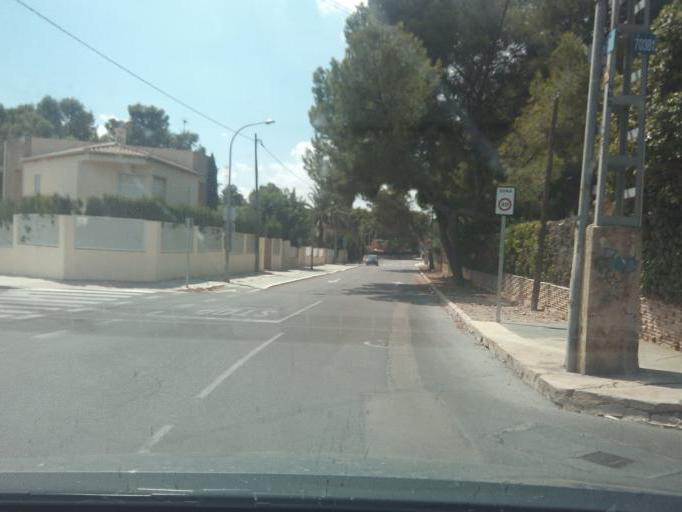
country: ES
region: Valencia
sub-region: Provincia de Valencia
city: Manises
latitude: 39.5351
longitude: -0.4846
